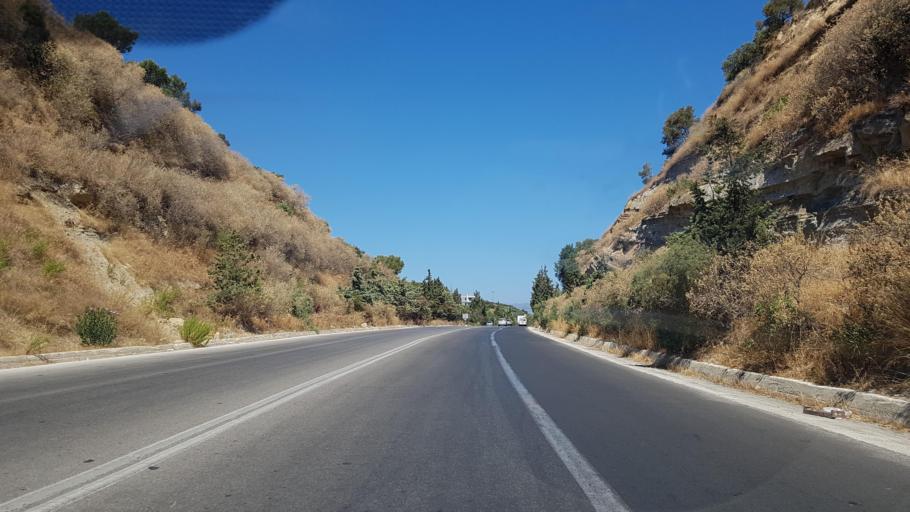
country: GR
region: Crete
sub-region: Nomos Chanias
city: Agia Marina
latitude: 35.5082
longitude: 23.9353
